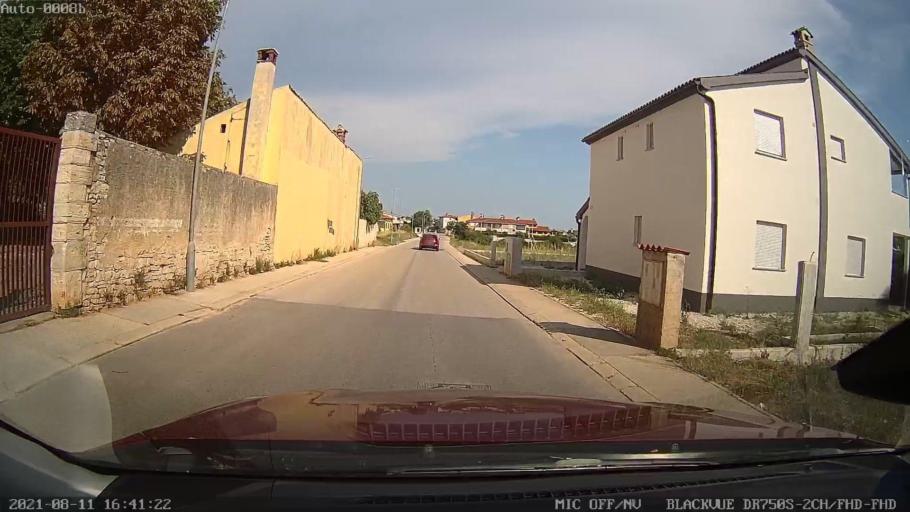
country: HR
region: Istarska
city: Vodnjan
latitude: 44.9558
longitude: 13.8449
